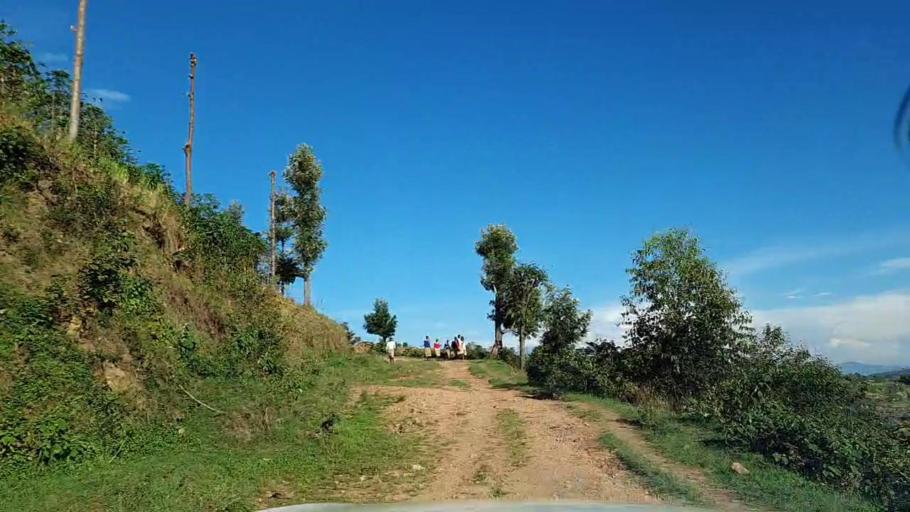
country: RW
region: Southern Province
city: Nzega
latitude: -2.4159
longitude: 29.5144
